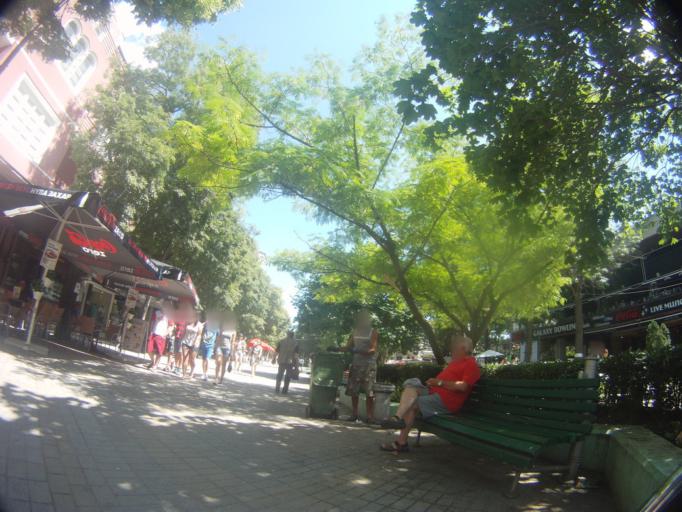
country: BG
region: Varna
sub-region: Obshtina Varna
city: Varna
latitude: 43.2051
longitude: 27.9205
